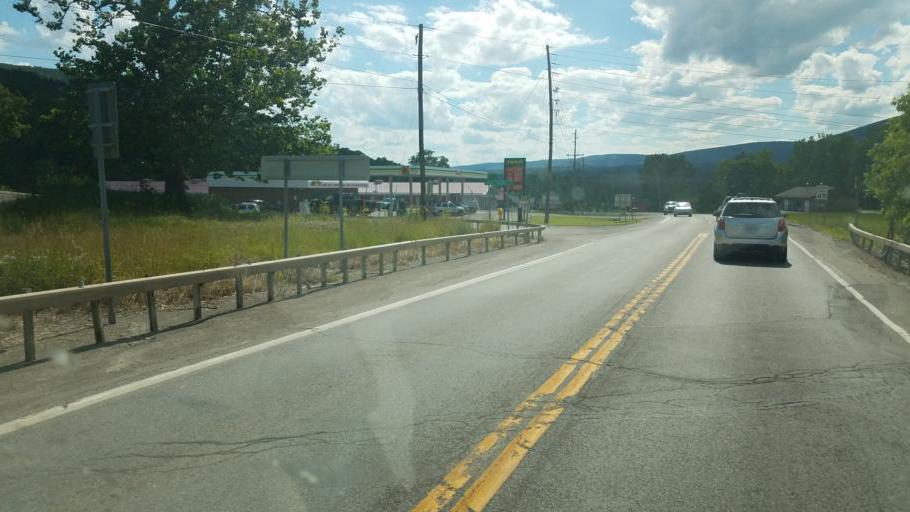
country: US
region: New York
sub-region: Steuben County
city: Bath
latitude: 42.4007
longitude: -77.2223
